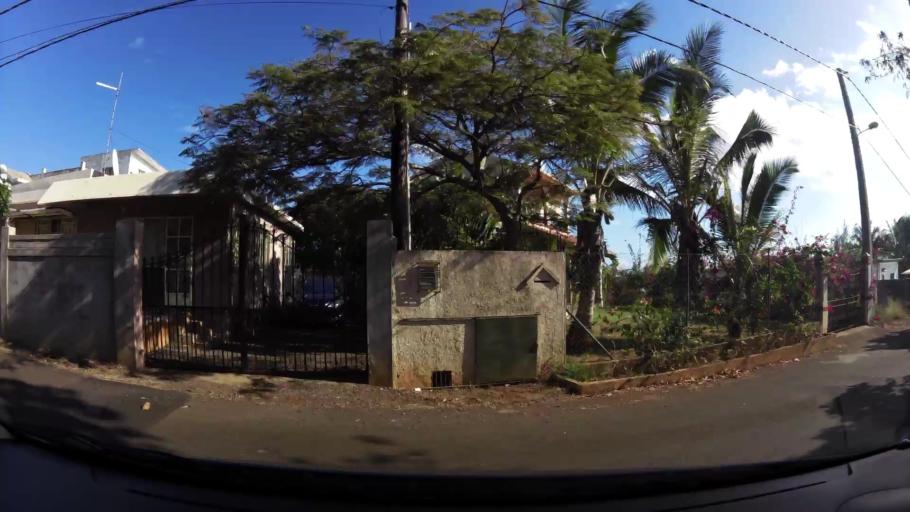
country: MU
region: Black River
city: Albion
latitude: -20.1976
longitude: 57.4079
